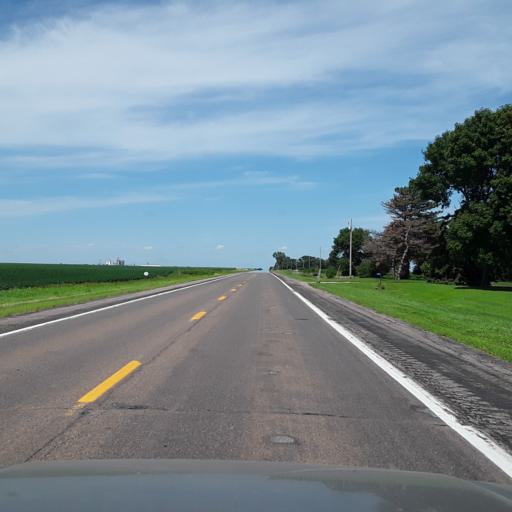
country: US
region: Nebraska
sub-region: Seward County
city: Seward
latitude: 40.9017
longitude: -97.1797
